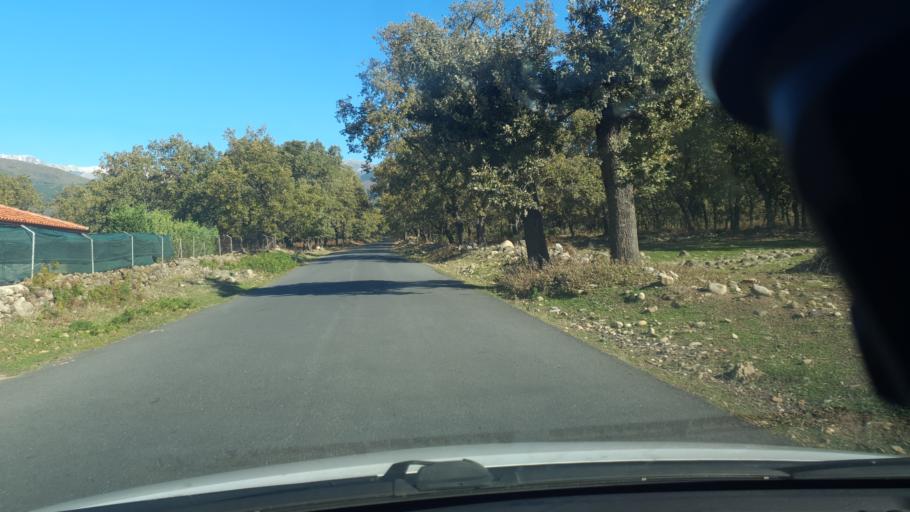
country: ES
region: Castille and Leon
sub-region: Provincia de Avila
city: Candeleda
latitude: 40.1342
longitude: -5.2632
